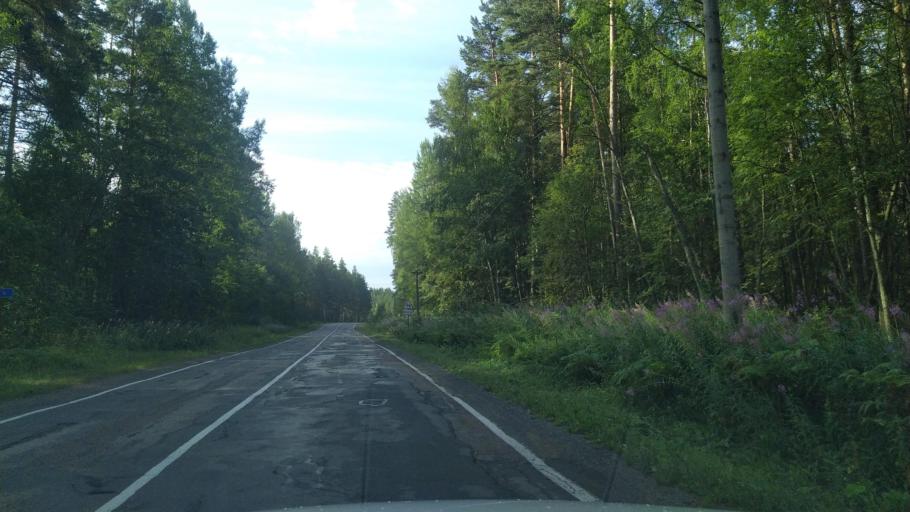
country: RU
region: Leningrad
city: Priozersk
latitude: 60.9831
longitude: 30.2676
